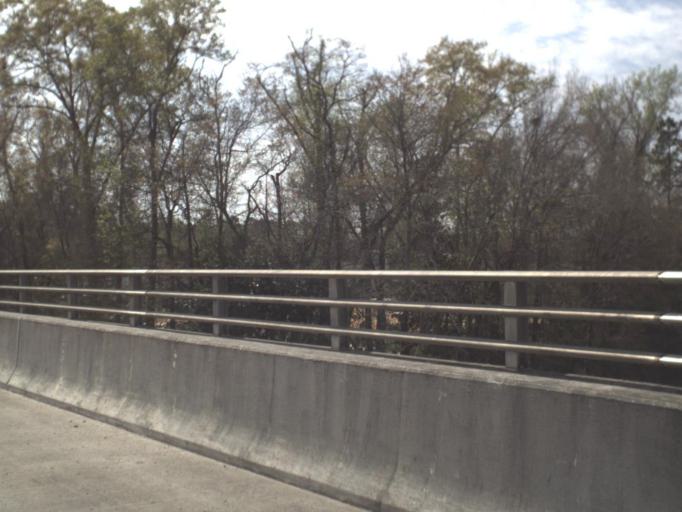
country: US
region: Florida
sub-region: Leon County
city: Tallahassee
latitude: 30.4543
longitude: -84.2266
